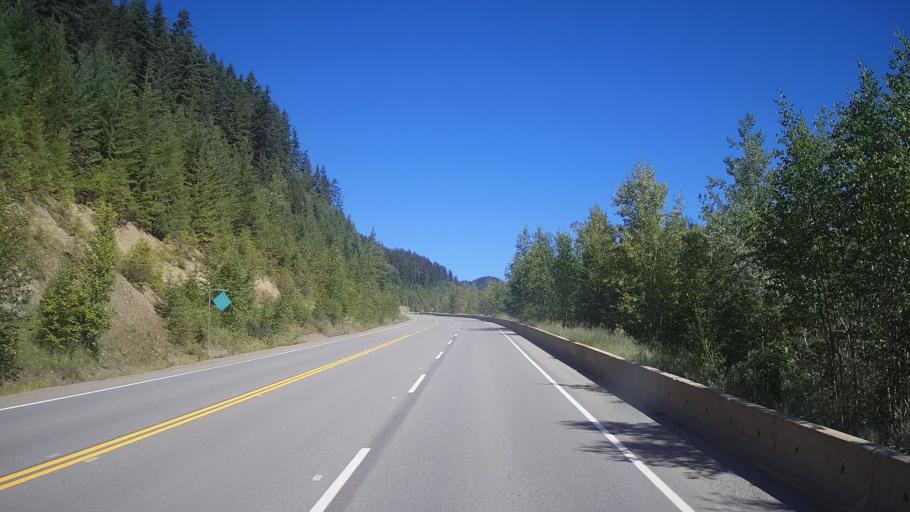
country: CA
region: British Columbia
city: Kamloops
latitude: 51.4803
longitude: -120.2602
